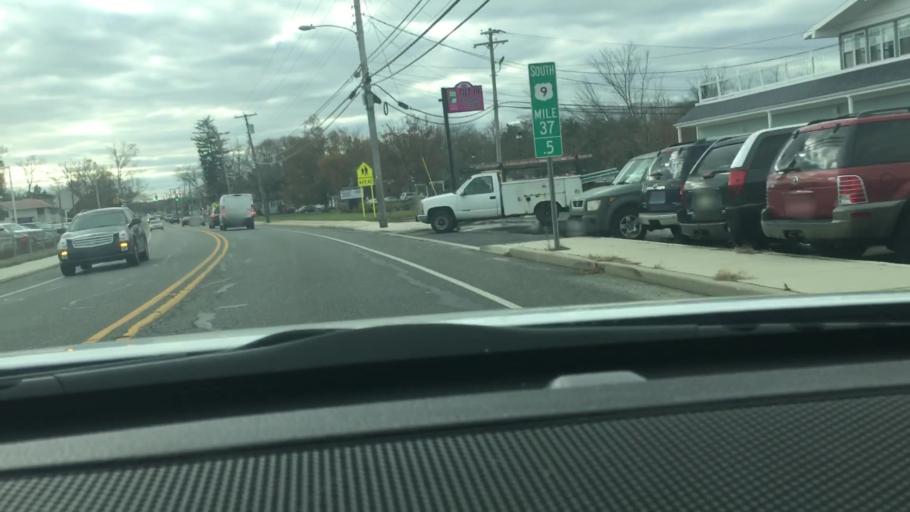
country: US
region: New Jersey
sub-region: Atlantic County
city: Northfield
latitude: 39.3678
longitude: -74.5615
